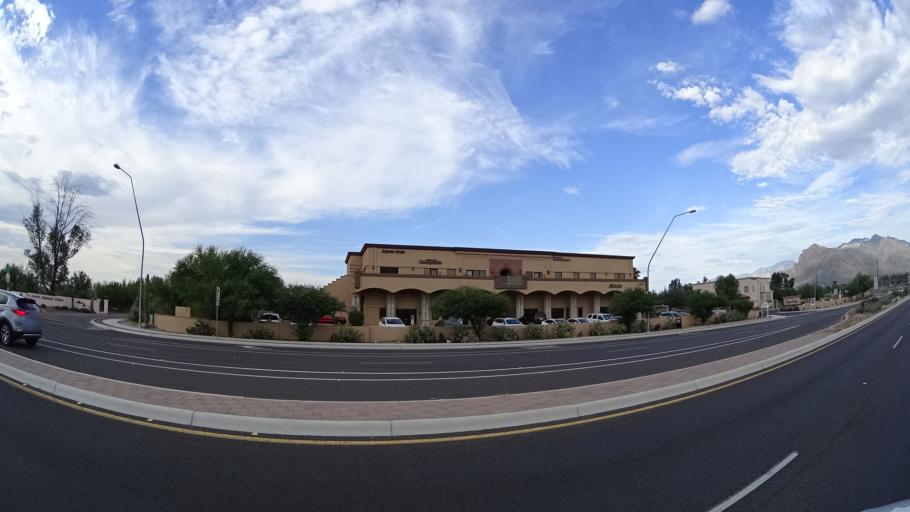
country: US
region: Arizona
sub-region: Pima County
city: Casas Adobes
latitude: 32.3469
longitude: -111.0172
